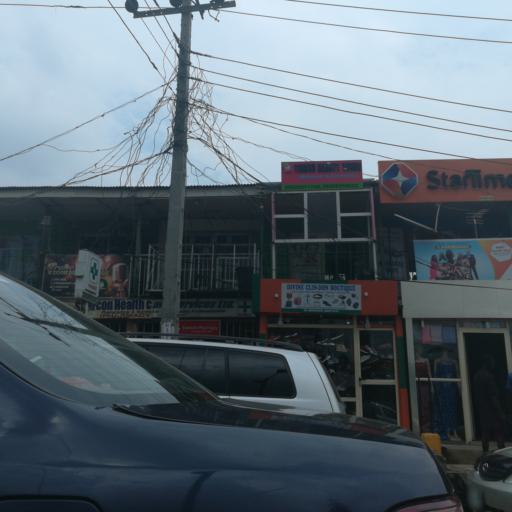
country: NG
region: Lagos
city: Ojota
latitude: 6.5869
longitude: 3.3832
